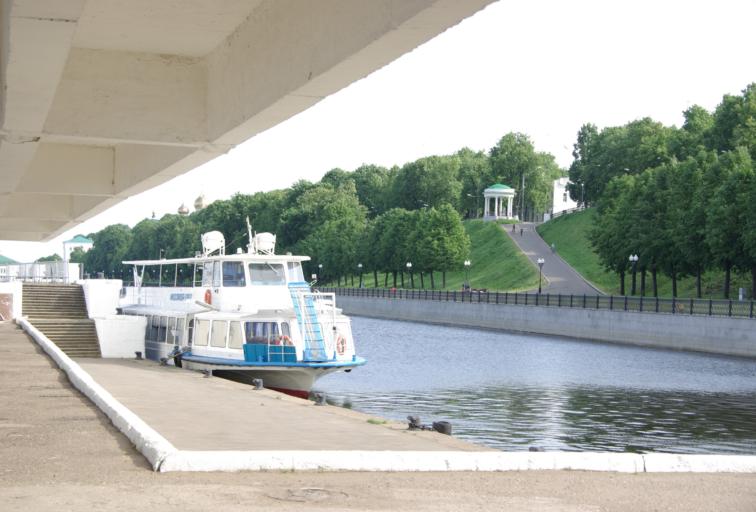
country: RU
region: Jaroslavl
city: Yaroslavl
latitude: 57.6317
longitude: 39.8886
